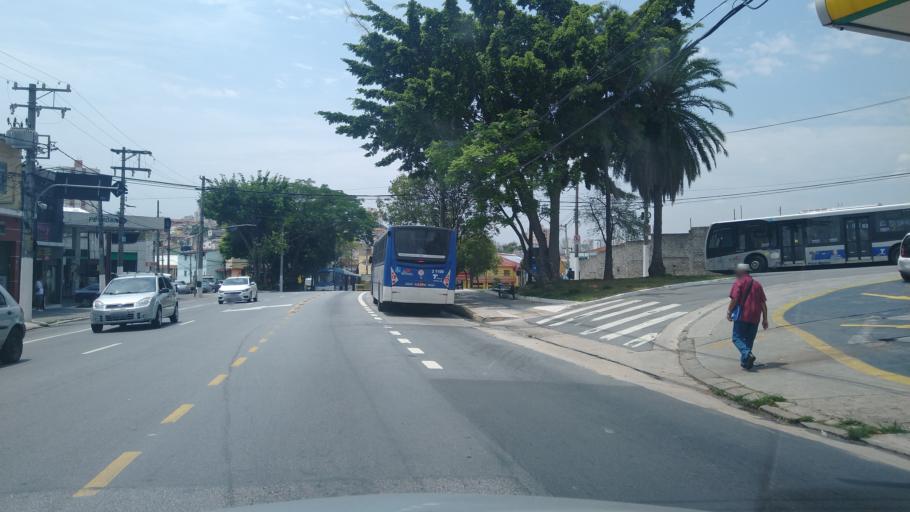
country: BR
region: Sao Paulo
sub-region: Sao Paulo
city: Sao Paulo
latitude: -23.4801
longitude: -46.6573
